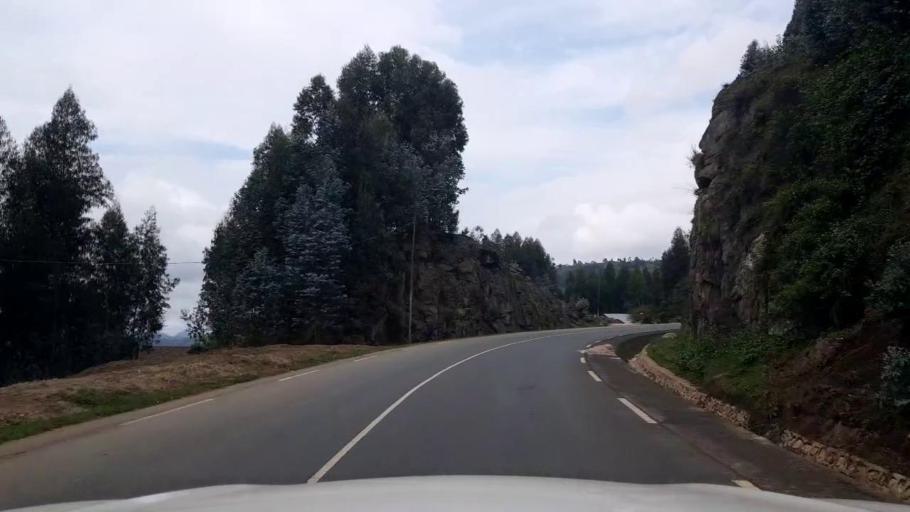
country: RW
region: Northern Province
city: Musanze
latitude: -1.6640
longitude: 29.5156
